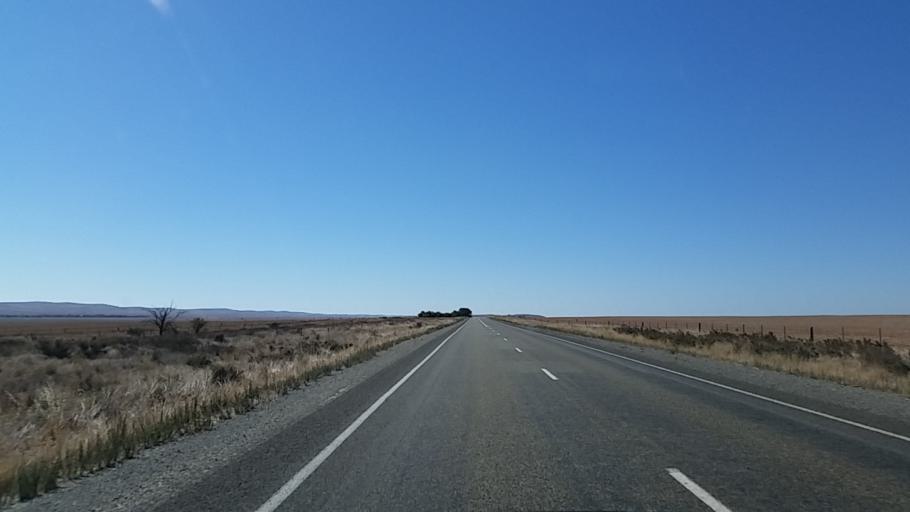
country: AU
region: South Australia
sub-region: Northern Areas
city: Jamestown
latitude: -33.2637
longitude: 138.8693
